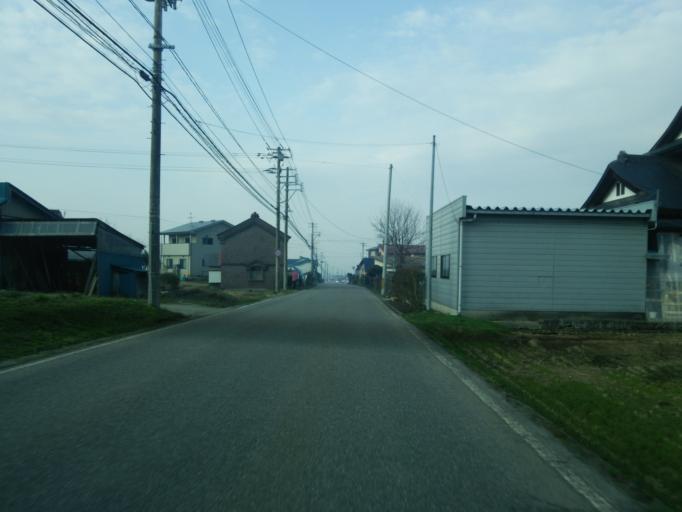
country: JP
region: Fukushima
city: Kitakata
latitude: 37.6867
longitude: 139.9044
